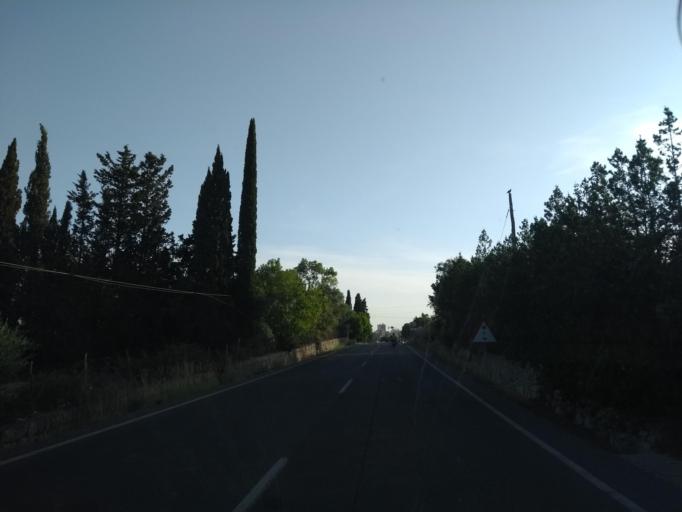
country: ES
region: Balearic Islands
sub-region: Illes Balears
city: Inca
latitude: 39.7288
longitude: 2.9272
